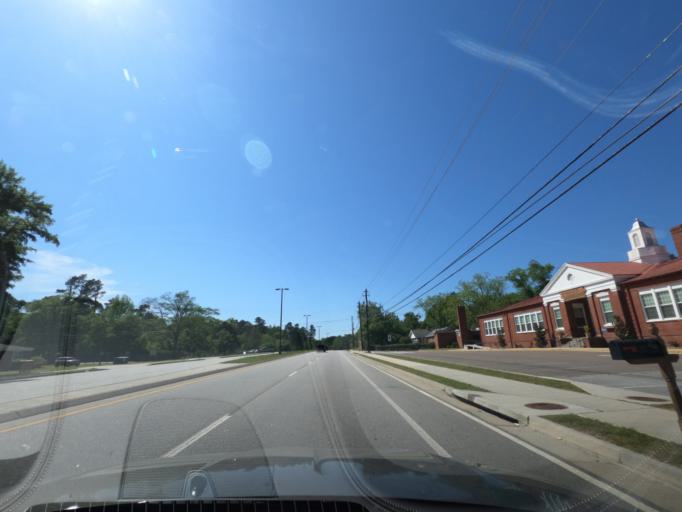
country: US
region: Georgia
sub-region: Columbia County
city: Martinez
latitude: 33.4698
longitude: -82.1005
